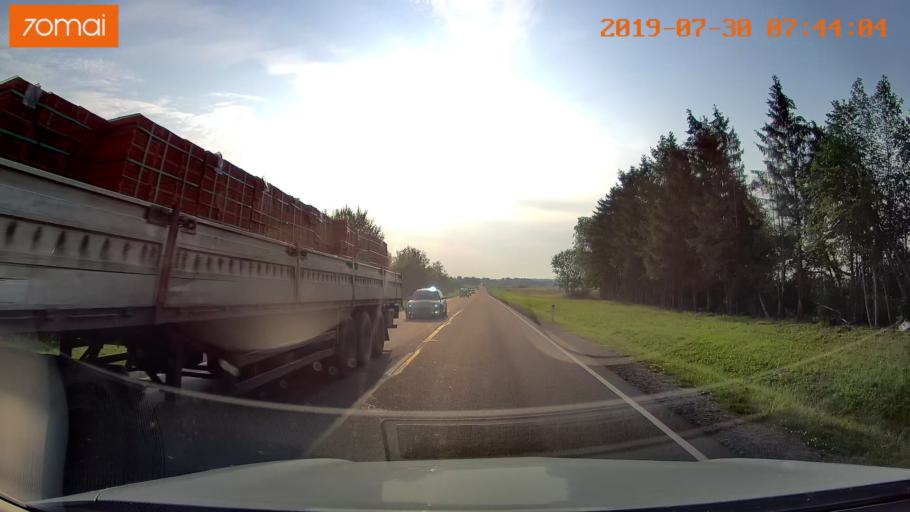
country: RU
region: Kaliningrad
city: Gvardeysk
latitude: 54.6496
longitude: 21.3166
